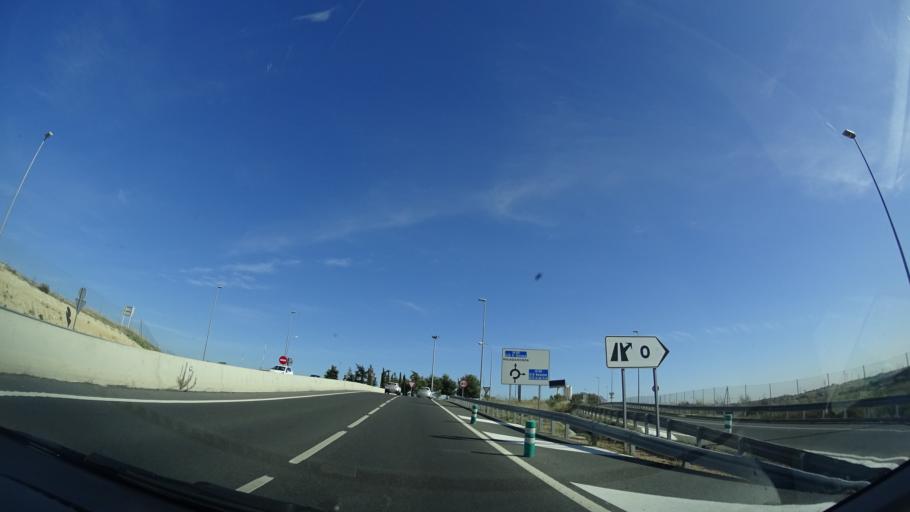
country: ES
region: Madrid
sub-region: Provincia de Madrid
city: Majadahonda
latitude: 40.4793
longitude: -3.8991
